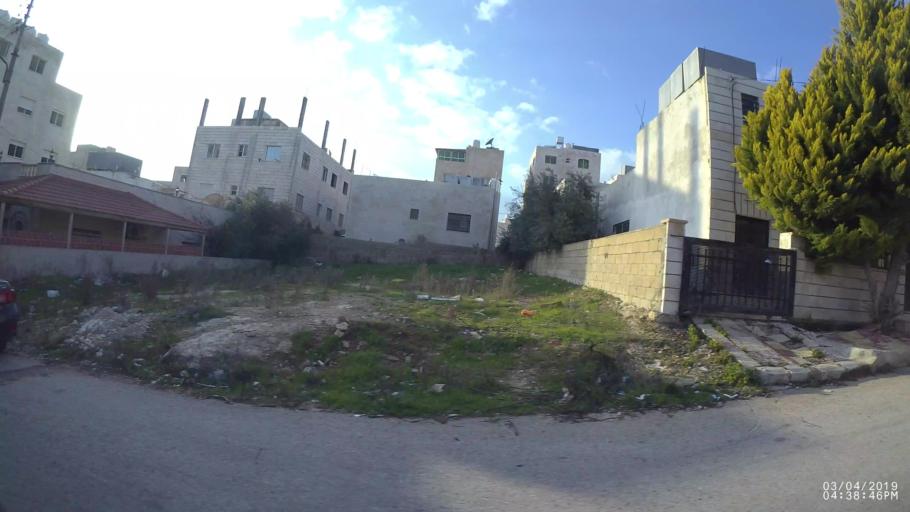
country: JO
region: Amman
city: Al Bunayyat ash Shamaliyah
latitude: 31.9131
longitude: 35.8920
